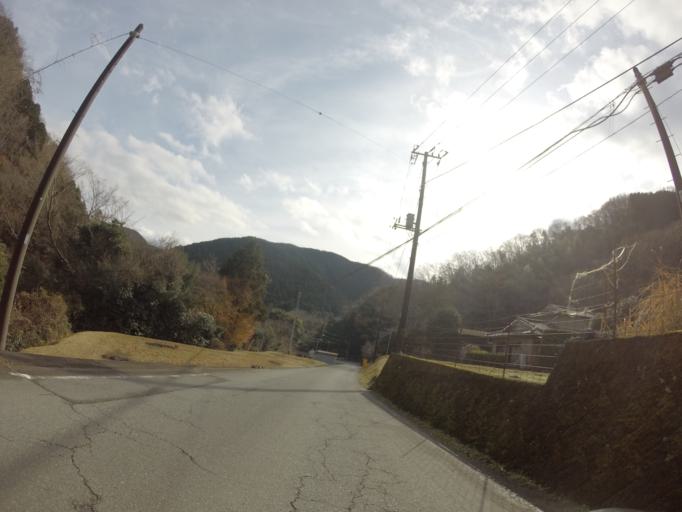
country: JP
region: Shizuoka
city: Heda
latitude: 34.8846
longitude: 138.9095
